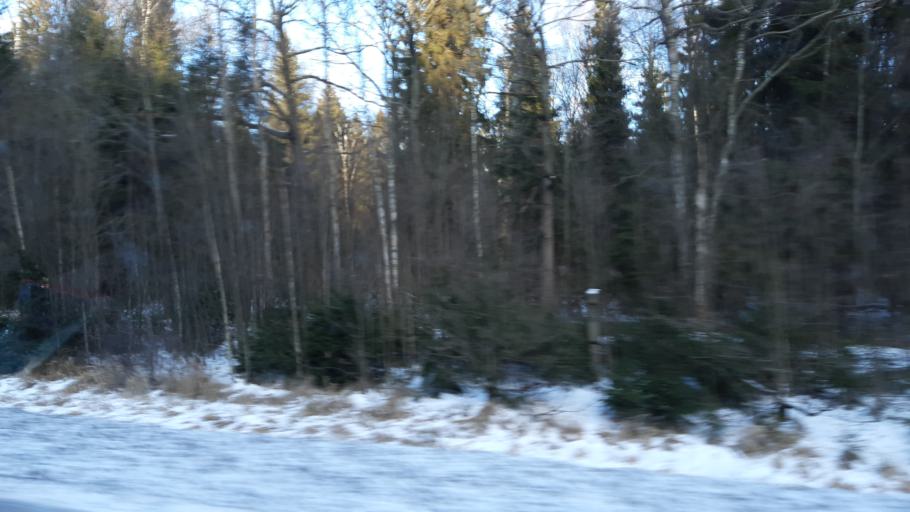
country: RU
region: Vladimir
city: Arsaki
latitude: 56.2723
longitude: 38.4165
